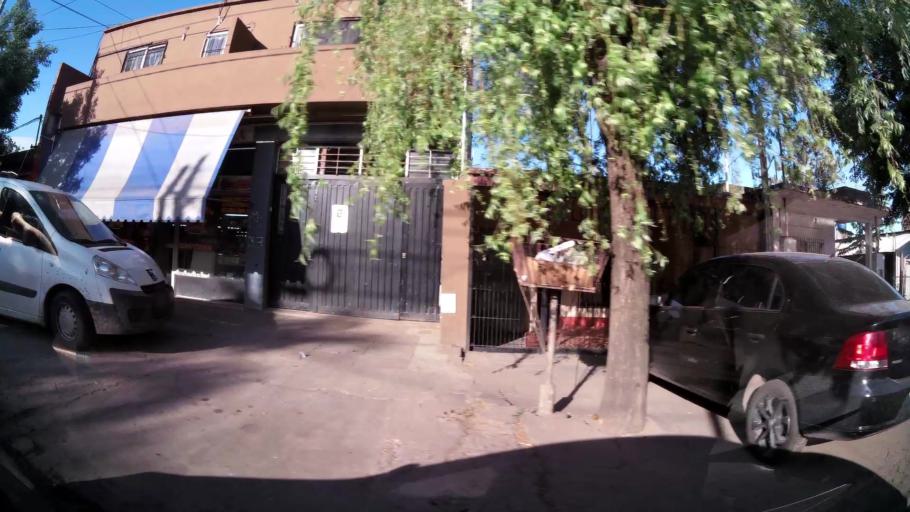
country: AR
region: Buenos Aires
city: Santa Catalina - Dique Lujan
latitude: -34.4708
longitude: -58.7386
